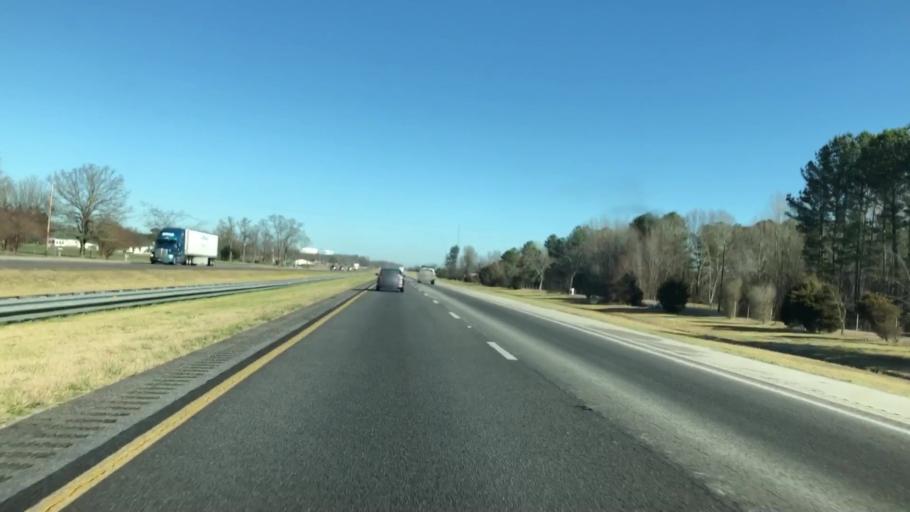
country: US
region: Alabama
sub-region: Limestone County
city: Athens
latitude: 34.8715
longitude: -86.9226
